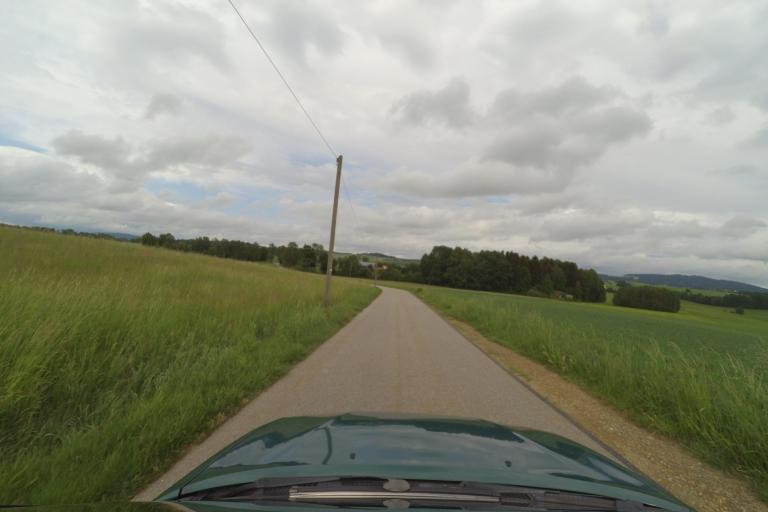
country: DE
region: Bavaria
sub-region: Upper Palatinate
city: Waldthurn
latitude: 49.6843
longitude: 12.2923
